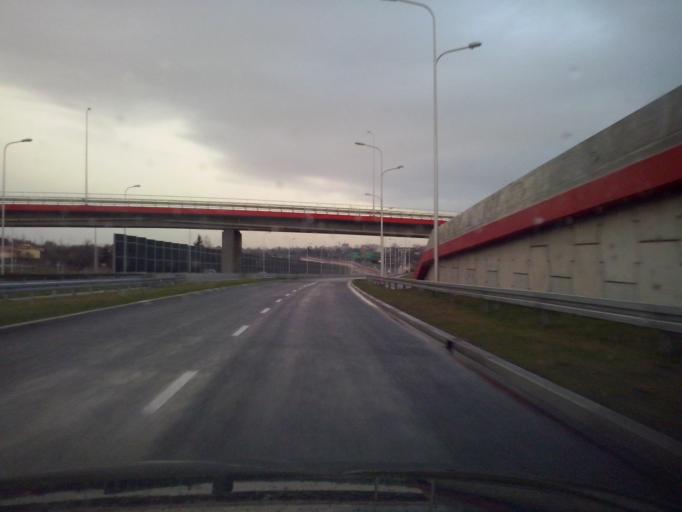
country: PL
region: Lublin Voivodeship
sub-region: Powiat lubelski
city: Jastkow
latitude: 51.2650
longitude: 22.4923
